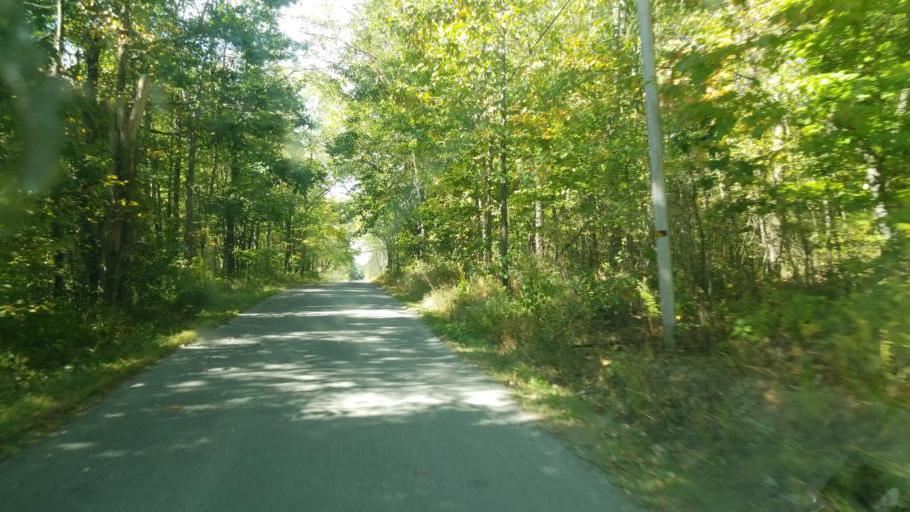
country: US
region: Pennsylvania
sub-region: Mercer County
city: Mercer
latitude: 41.3468
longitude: -80.2542
